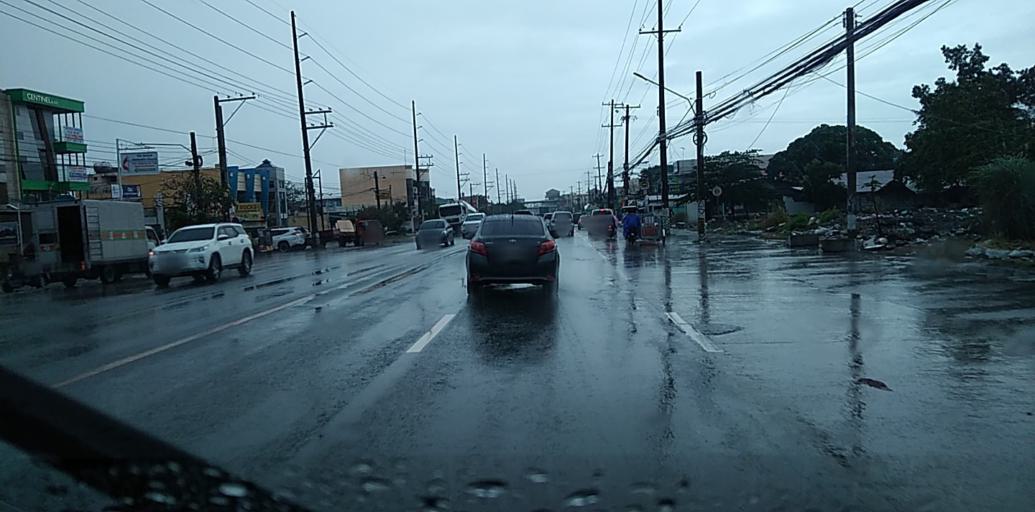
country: PH
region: Central Luzon
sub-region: Province of Pampanga
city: Magliman
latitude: 15.0561
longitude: 120.6595
